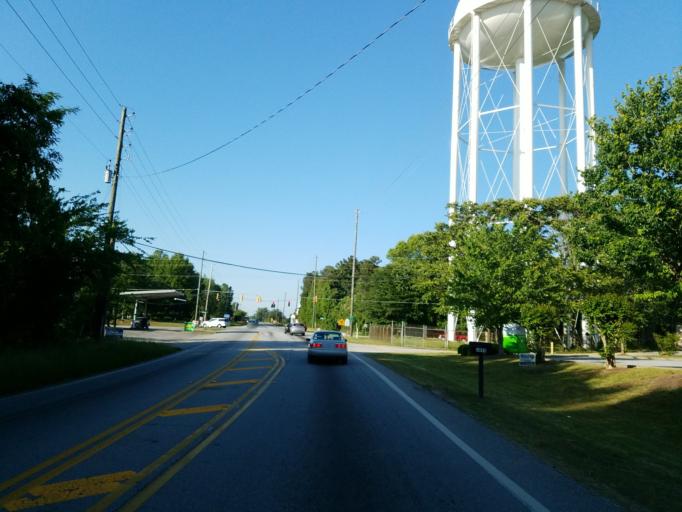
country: US
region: Georgia
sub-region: Douglas County
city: Douglasville
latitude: 33.7763
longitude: -84.7065
